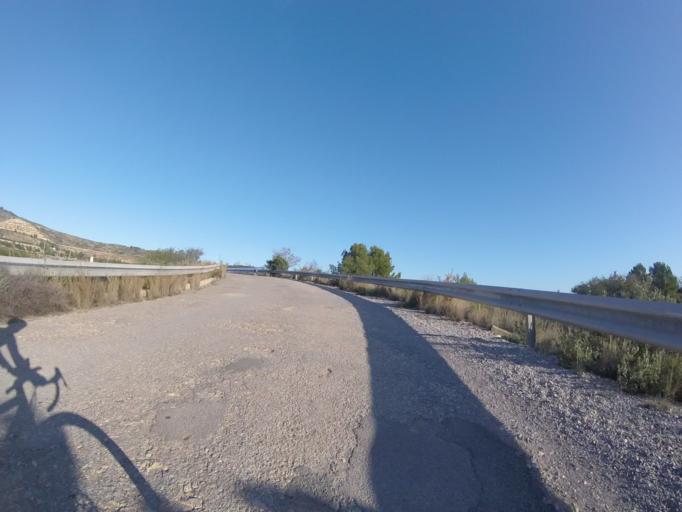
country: ES
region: Valencia
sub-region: Provincia de Castello
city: Torreblanca
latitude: 40.2255
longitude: 0.1984
